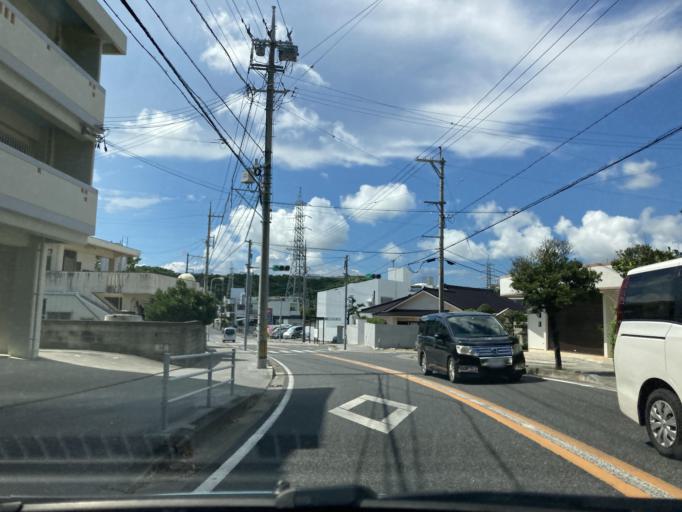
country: JP
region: Okinawa
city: Tomigusuku
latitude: 26.1691
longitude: 127.7207
